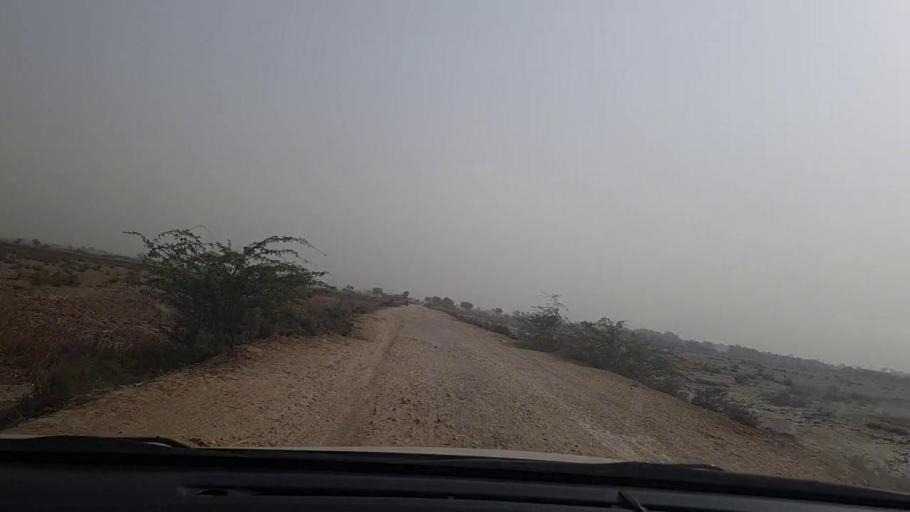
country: PK
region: Sindh
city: Pithoro
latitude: 25.4129
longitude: 69.3171
